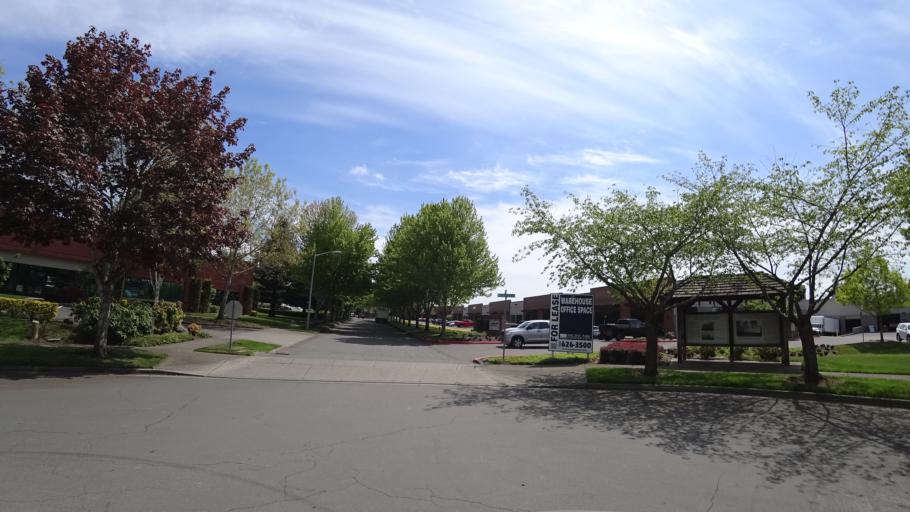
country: US
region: Oregon
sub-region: Washington County
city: Rockcreek
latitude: 45.5644
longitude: -122.9225
